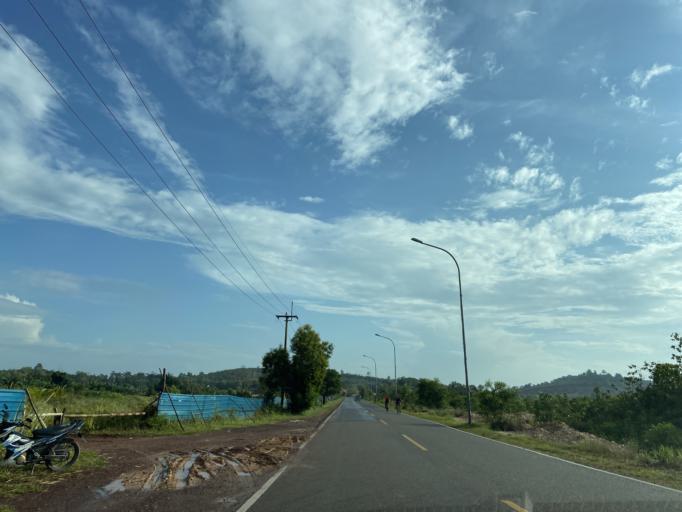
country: SG
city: Singapore
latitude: 0.9529
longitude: 104.0525
